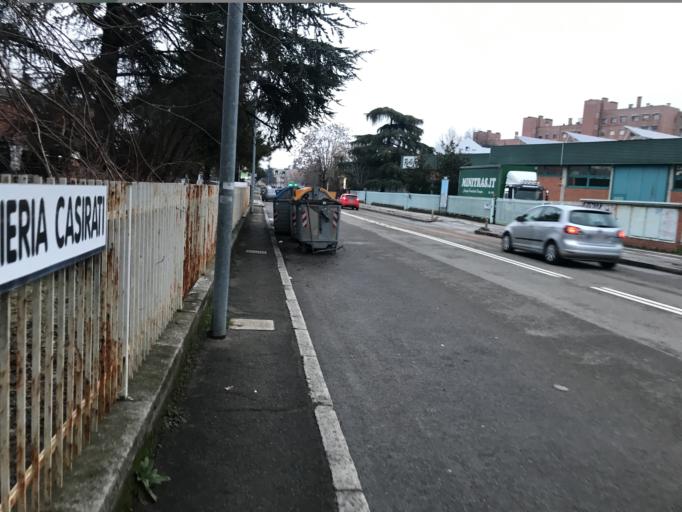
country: IT
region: Emilia-Romagna
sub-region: Provincia di Bologna
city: Progresso
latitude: 44.5356
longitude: 11.3493
